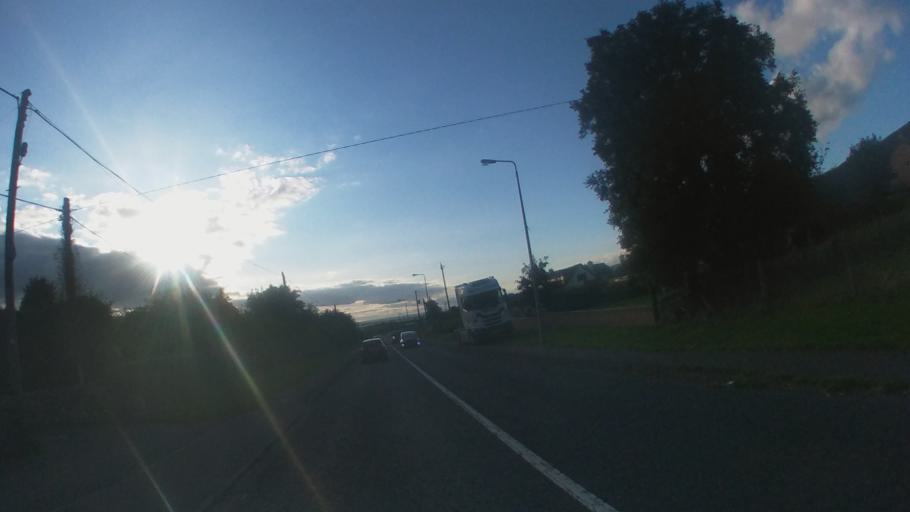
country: IE
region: Leinster
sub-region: Lu
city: Carlingford
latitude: 54.0012
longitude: -6.2718
